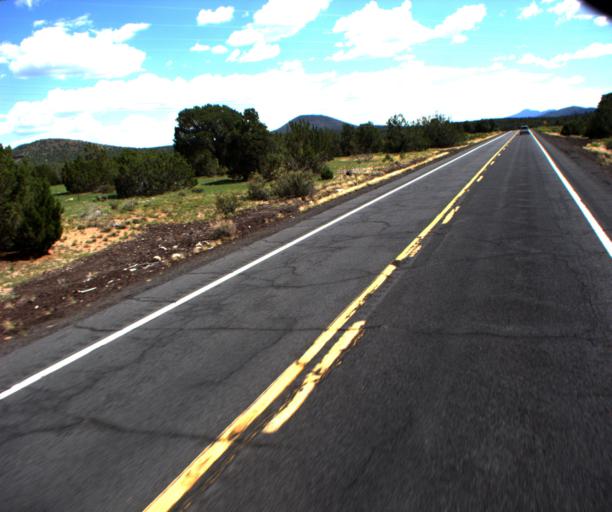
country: US
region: Arizona
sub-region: Coconino County
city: Williams
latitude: 35.4495
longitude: -112.1712
